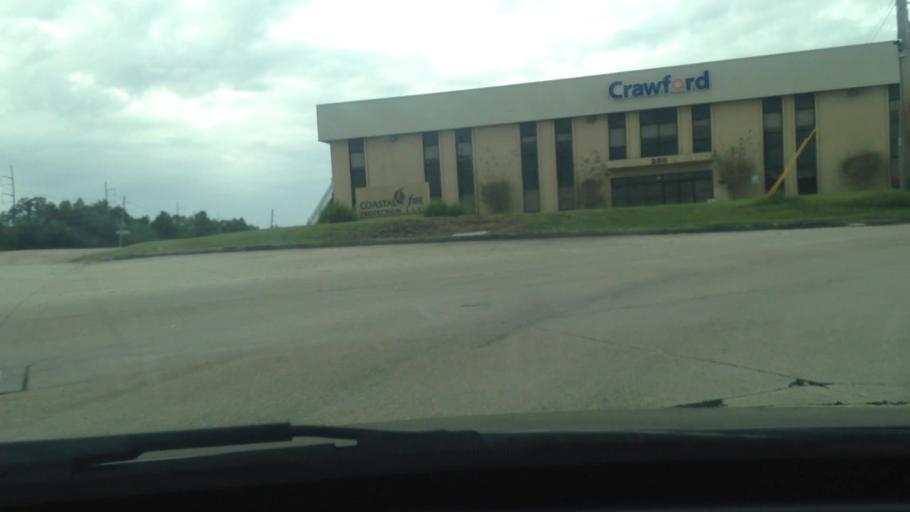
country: US
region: Louisiana
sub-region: Jefferson Parish
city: Jefferson
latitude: 29.9716
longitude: -90.1277
